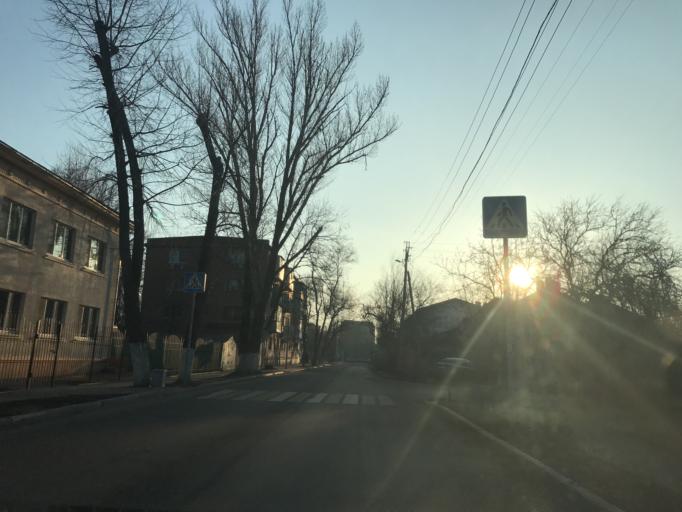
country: RU
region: Rostov
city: Rostov-na-Donu
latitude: 47.2139
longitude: 39.6615
